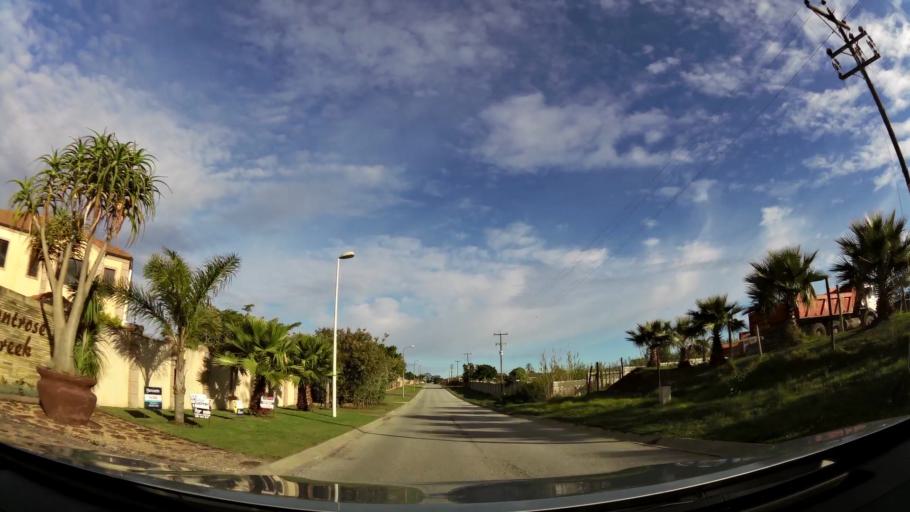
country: ZA
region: Eastern Cape
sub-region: Nelson Mandela Bay Metropolitan Municipality
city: Port Elizabeth
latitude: -33.9549
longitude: 25.4877
